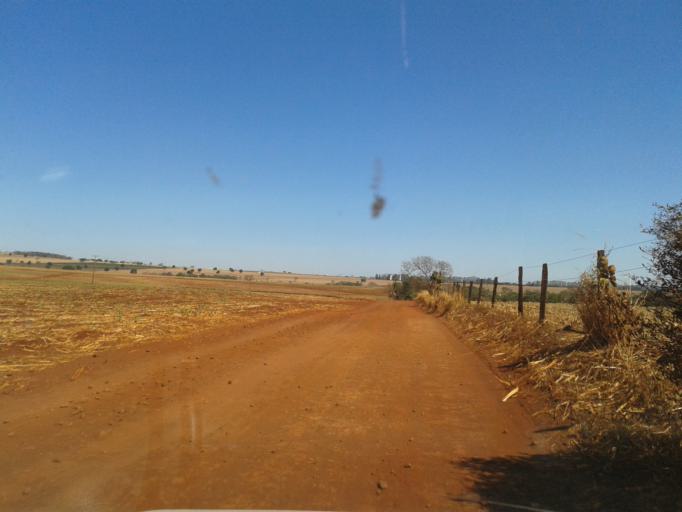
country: BR
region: Minas Gerais
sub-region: Centralina
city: Centralina
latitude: -18.5905
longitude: -49.1636
